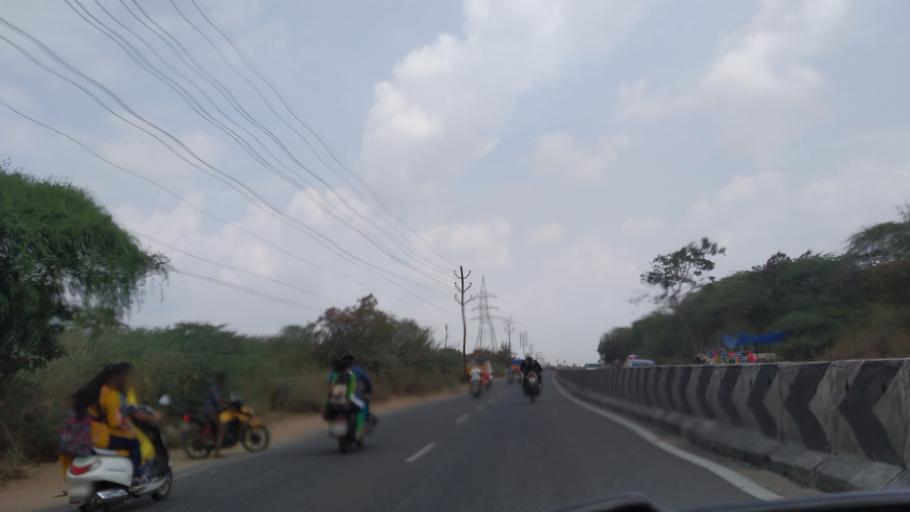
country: IN
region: Tamil Nadu
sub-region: Coimbatore
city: Madukkarai
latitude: 10.9242
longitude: 76.9491
